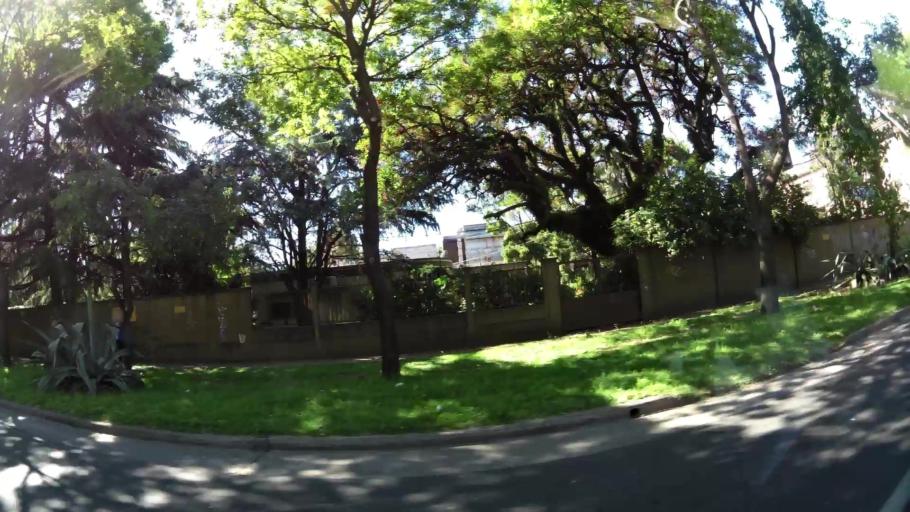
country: AR
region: Buenos Aires
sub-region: Partido de General San Martin
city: General San Martin
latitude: -34.5402
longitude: -58.5247
